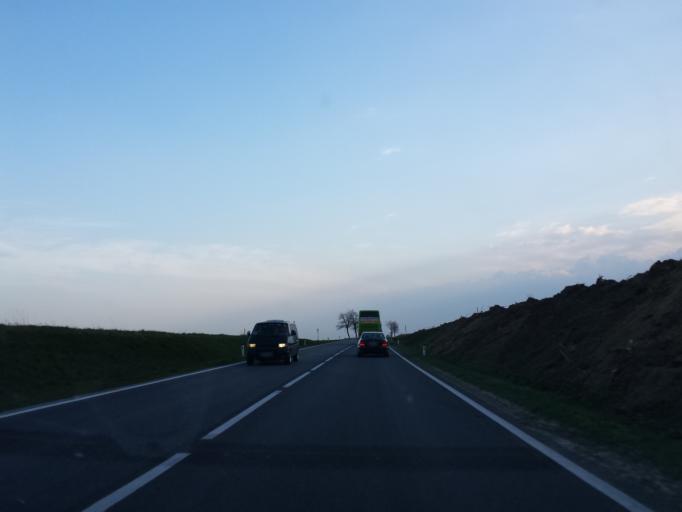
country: AT
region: Lower Austria
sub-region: Politischer Bezirk Mistelbach
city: Wilfersdorf
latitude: 48.6027
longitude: 16.6475
